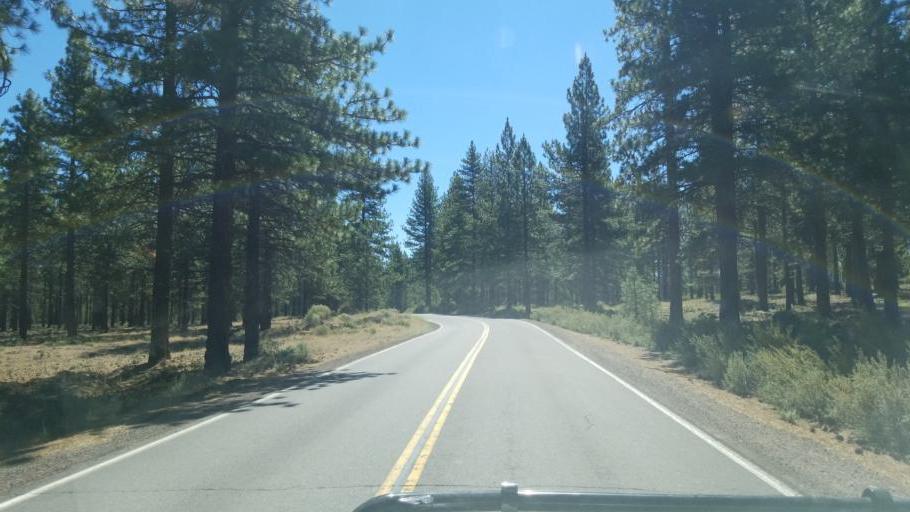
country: US
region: California
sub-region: Lassen County
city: Susanville
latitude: 40.4226
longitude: -120.7180
